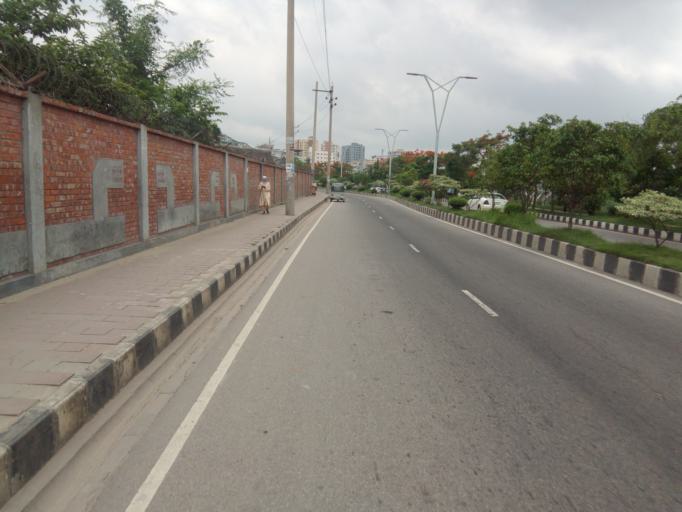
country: BD
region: Dhaka
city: Paltan
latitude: 23.7558
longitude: 90.4046
